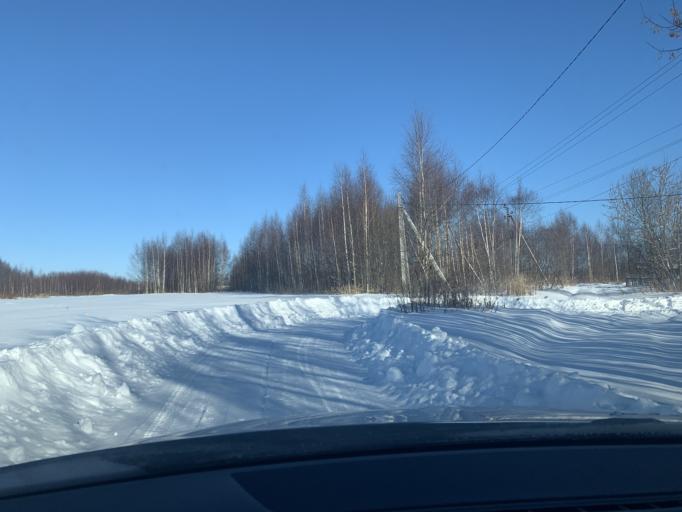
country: RU
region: Jaroslavl
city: Tunoshna
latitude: 57.6527
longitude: 40.0604
